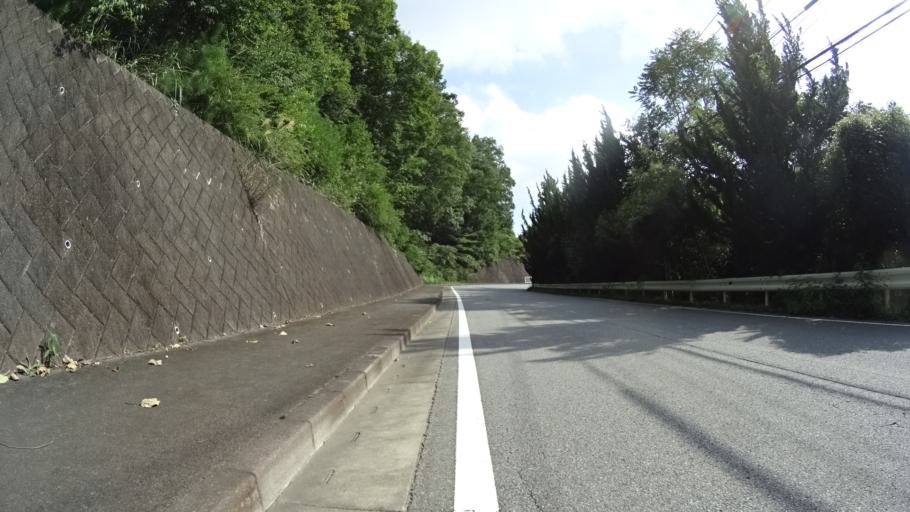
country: JP
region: Yamanashi
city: Kofu-shi
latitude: 35.7089
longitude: 138.5531
